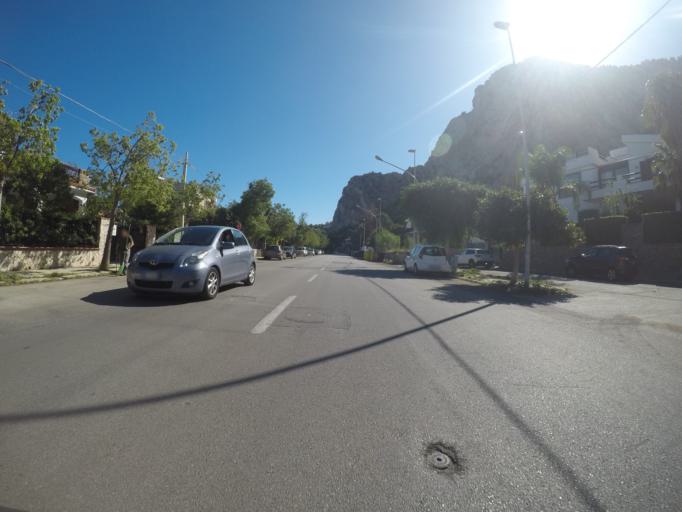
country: IT
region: Sicily
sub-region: Palermo
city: Palermo
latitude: 38.1888
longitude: 13.3489
